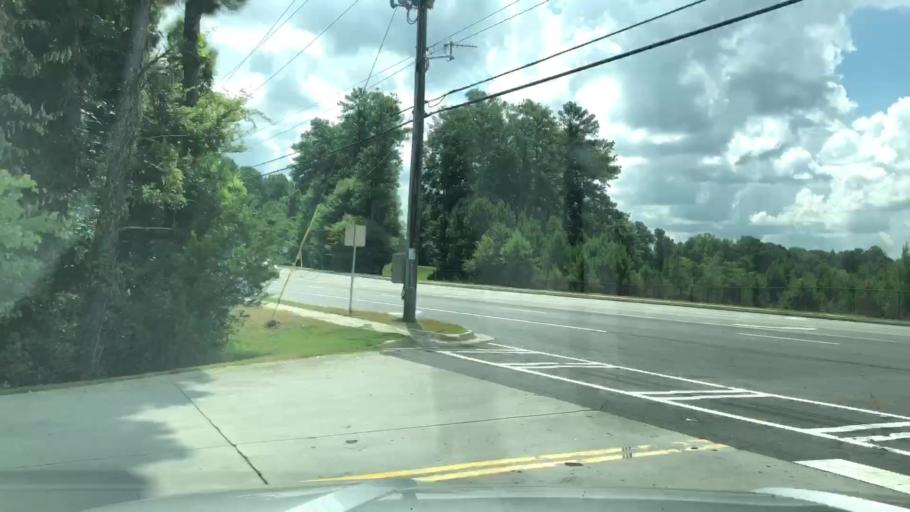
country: US
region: Georgia
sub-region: Fulton County
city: Union City
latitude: 33.5838
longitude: -84.5089
